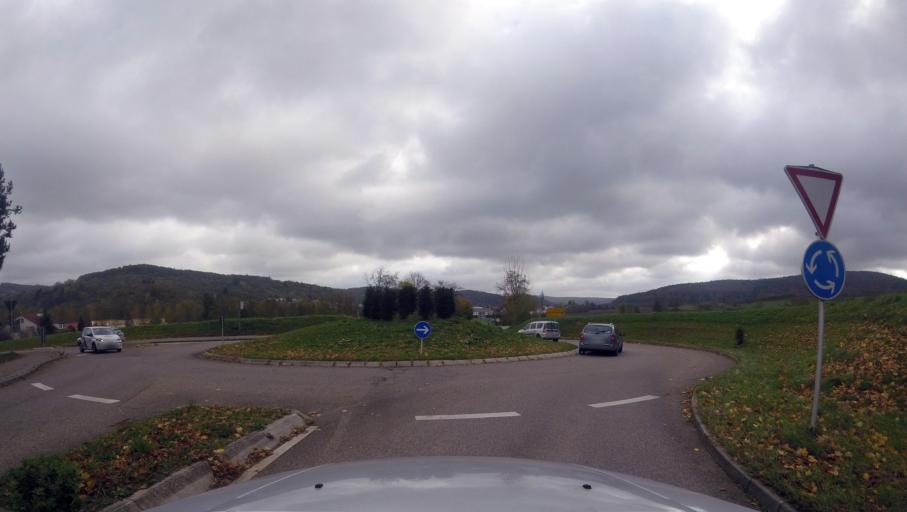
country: DE
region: Baden-Wuerttemberg
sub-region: Regierungsbezirk Stuttgart
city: Winnenden
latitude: 48.8699
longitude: 9.4186
